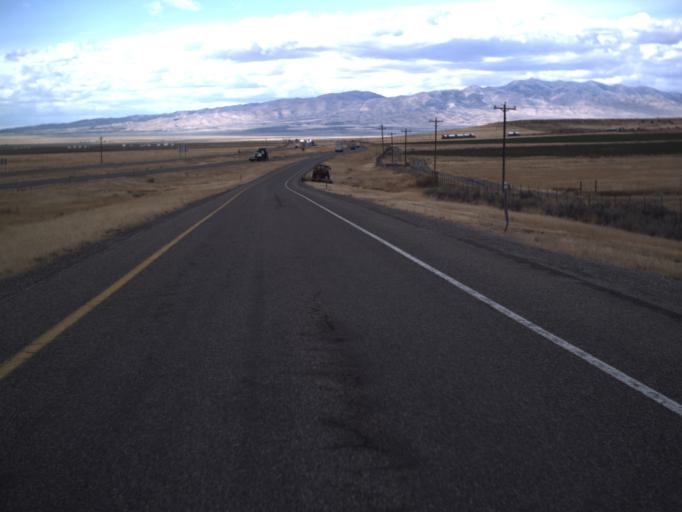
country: US
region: Idaho
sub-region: Oneida County
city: Malad City
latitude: 41.9662
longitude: -112.7580
